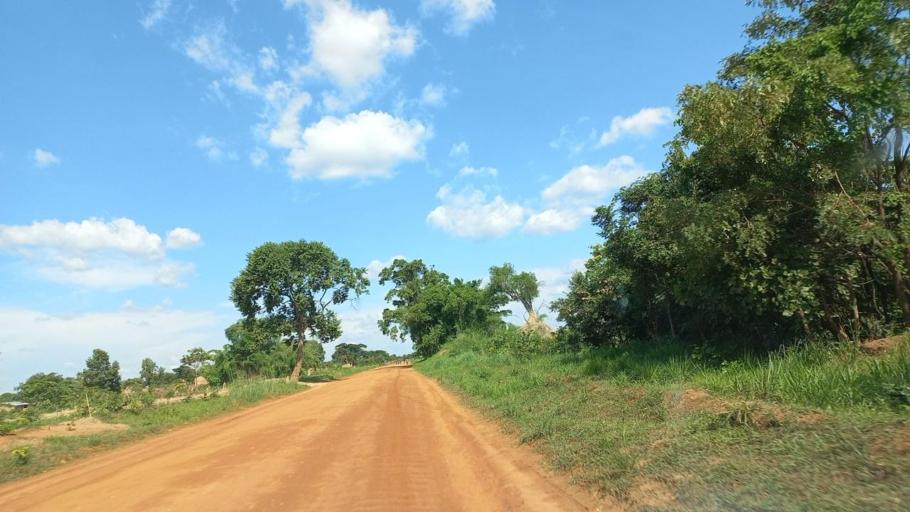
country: ZM
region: Copperbelt
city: Kitwe
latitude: -12.8702
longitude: 28.3537
